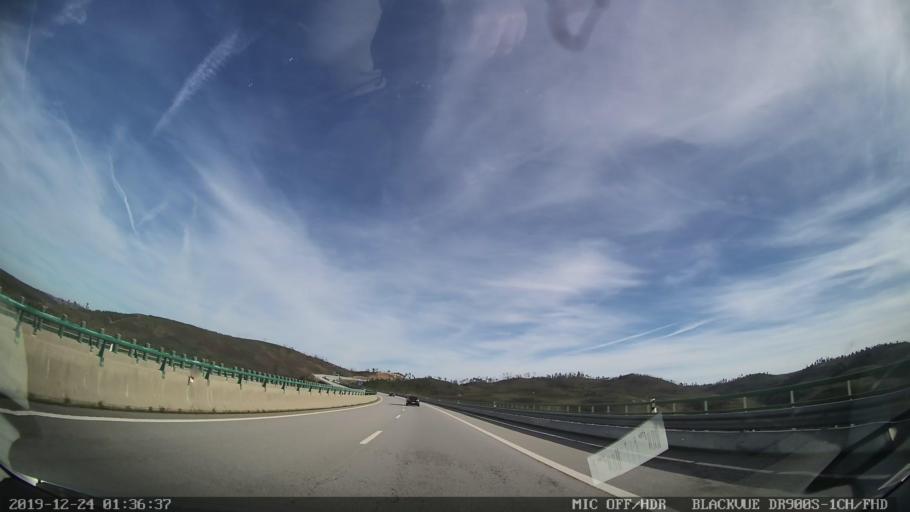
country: PT
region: Santarem
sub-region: Macao
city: Macao
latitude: 39.5227
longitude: -7.9788
